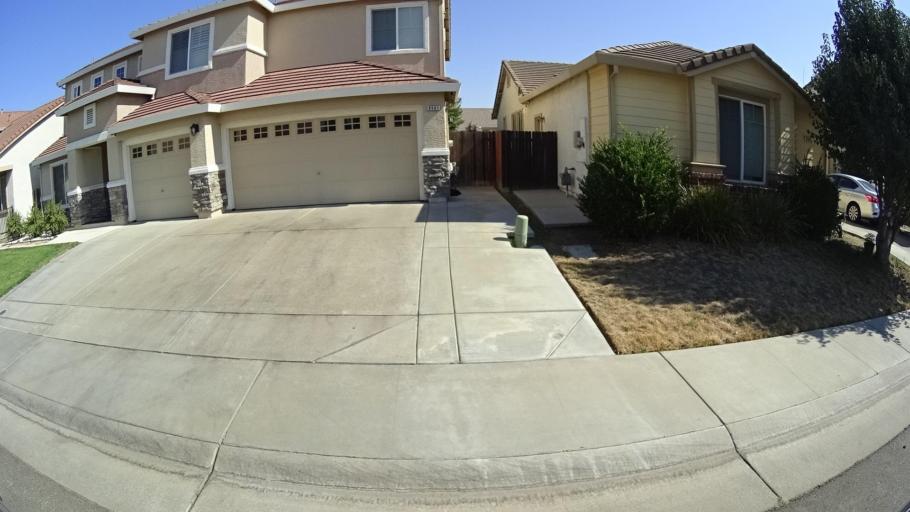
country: US
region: California
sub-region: Sacramento County
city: Laguna
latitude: 38.4466
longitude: -121.3953
